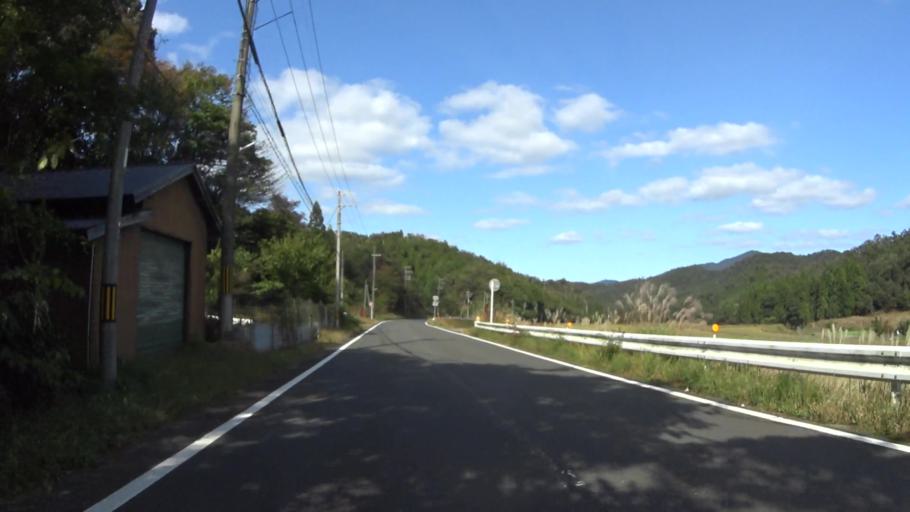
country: JP
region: Hyogo
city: Toyooka
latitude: 35.5521
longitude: 134.9767
